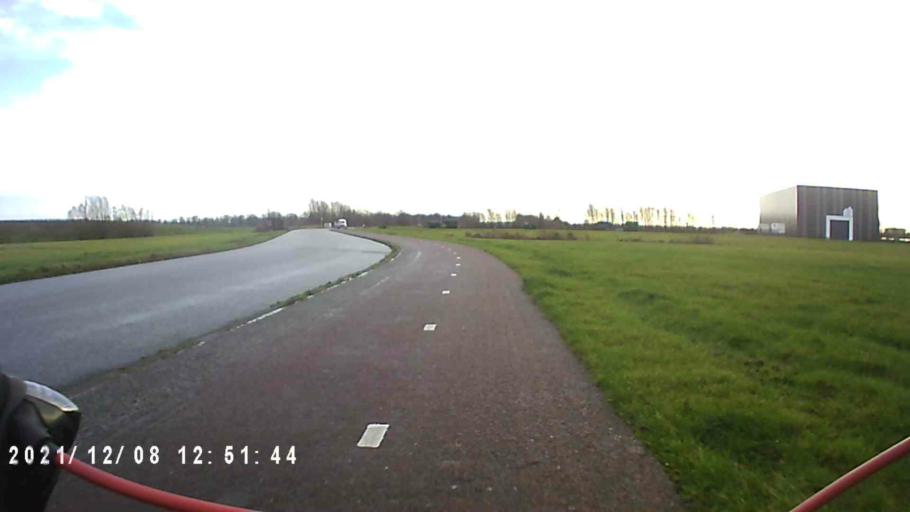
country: NL
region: Groningen
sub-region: Gemeente Haren
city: Haren
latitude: 53.2037
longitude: 6.6281
